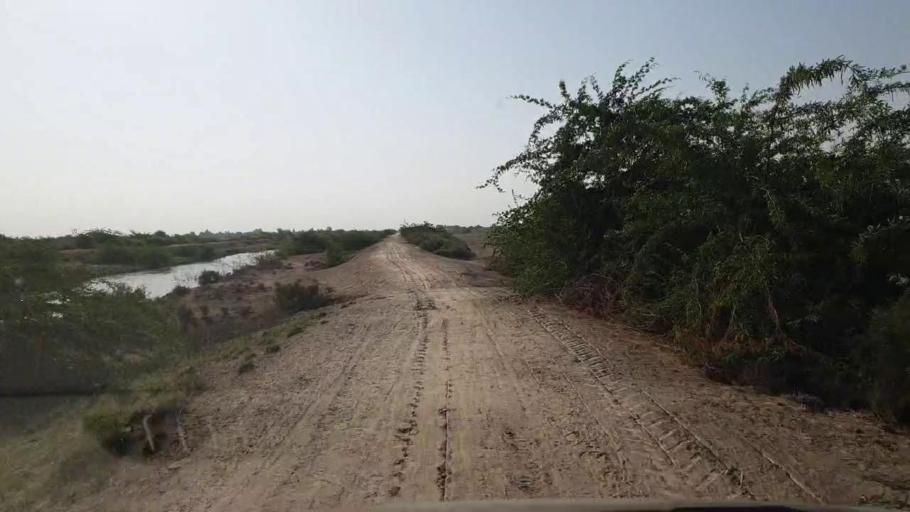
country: PK
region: Sindh
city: Kadhan
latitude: 24.5840
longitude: 69.0787
